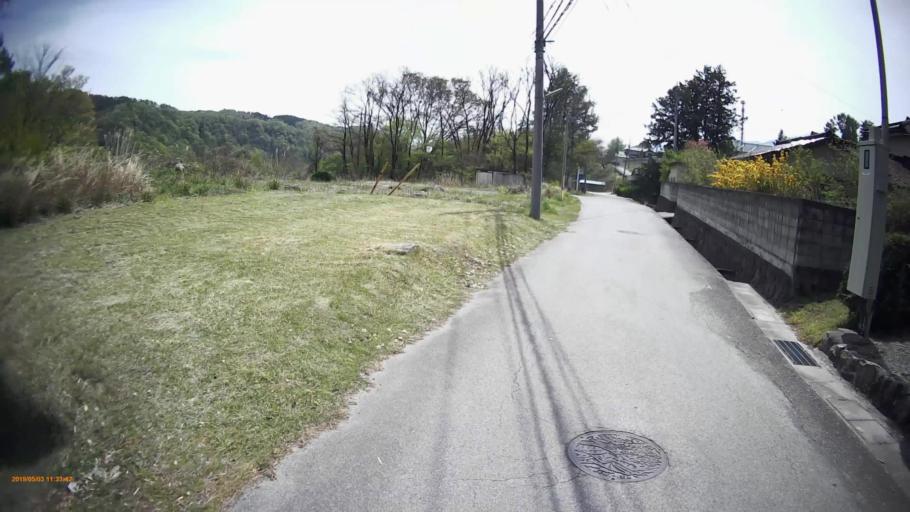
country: JP
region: Nagano
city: Chino
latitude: 35.8463
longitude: 138.2995
